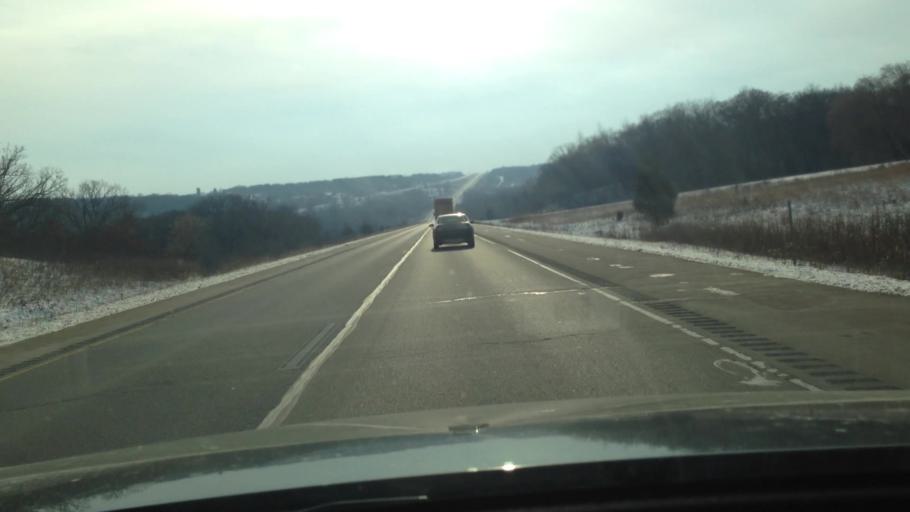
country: US
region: Wisconsin
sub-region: Walworth County
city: East Troy
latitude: 42.7323
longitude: -88.4607
